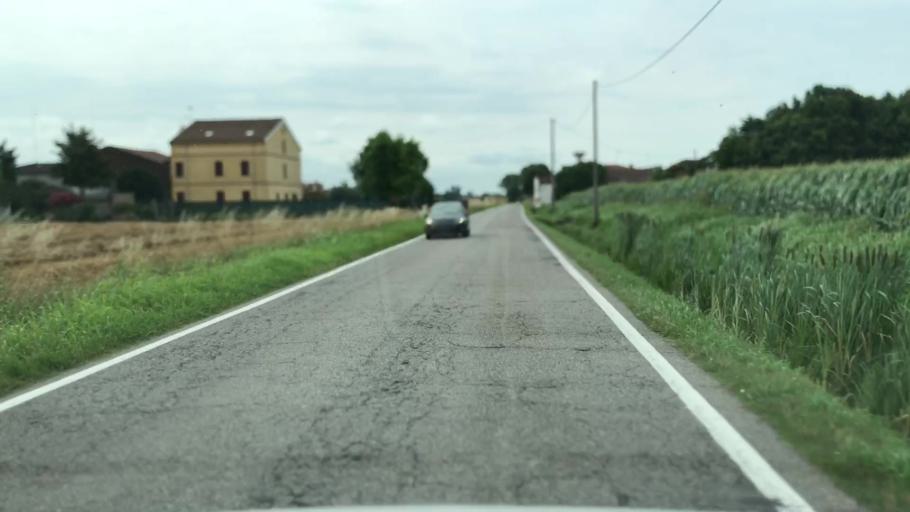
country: IT
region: Lombardy
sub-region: Provincia di Mantova
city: Quistello
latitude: 45.0229
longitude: 10.9927
